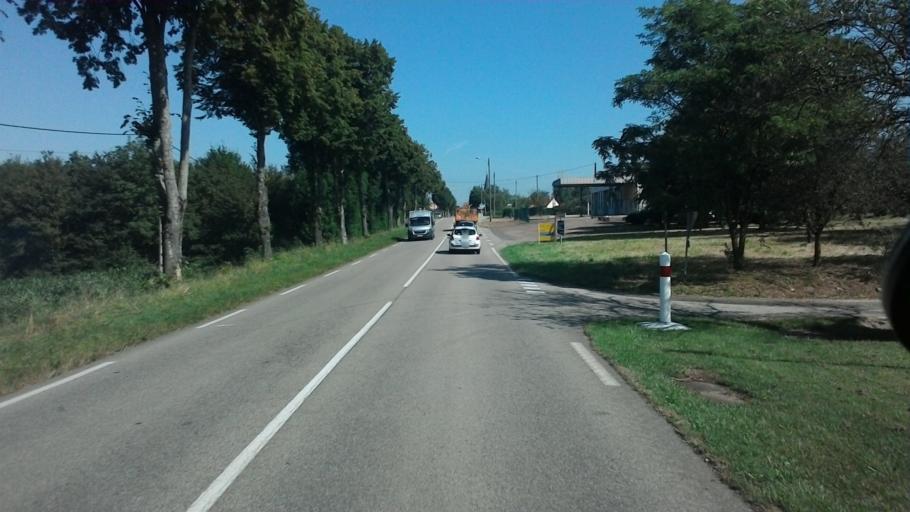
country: FR
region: Rhone-Alpes
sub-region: Departement de l'Ain
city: Saint-Trivier-de-Courtes
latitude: 46.4539
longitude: 5.0852
